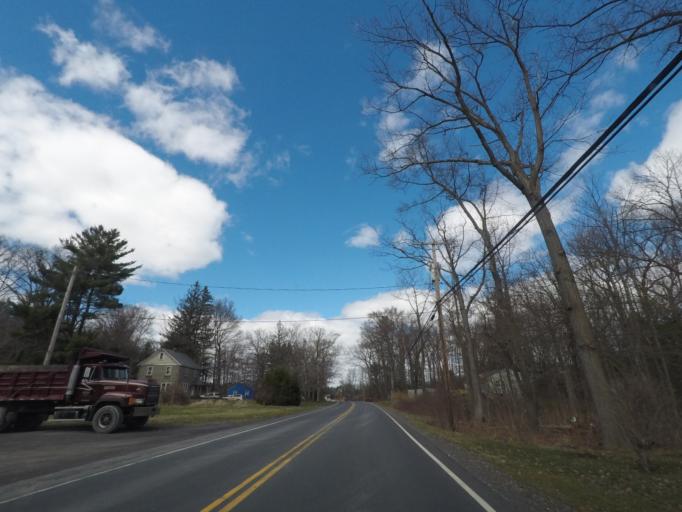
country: US
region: New York
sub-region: Albany County
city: Delmar
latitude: 42.5780
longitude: -73.8299
